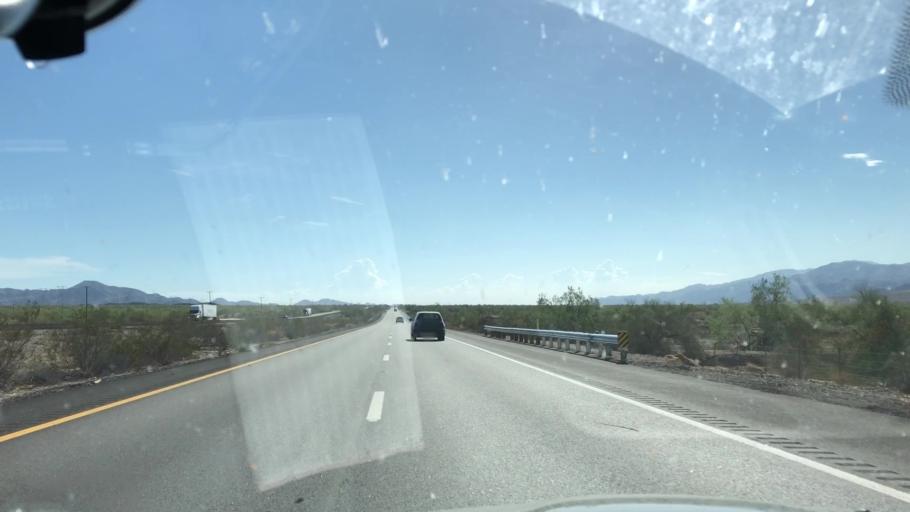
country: US
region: California
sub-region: Imperial County
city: Niland
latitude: 33.6934
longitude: -115.4948
